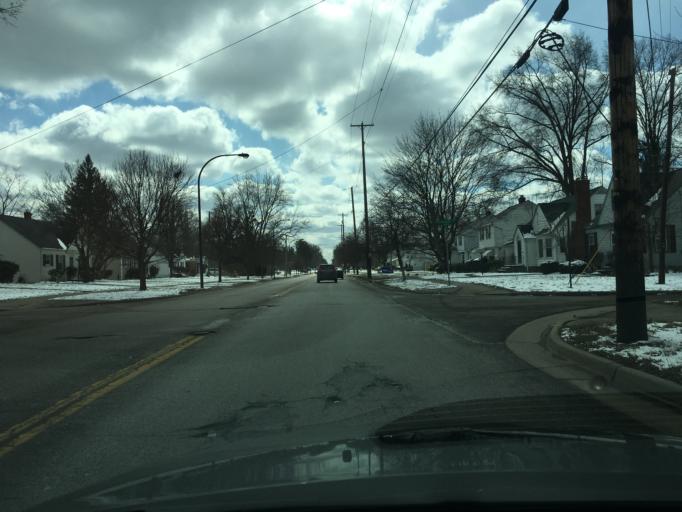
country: US
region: Ohio
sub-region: Summit County
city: Fairlawn
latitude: 41.1026
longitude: -81.5693
